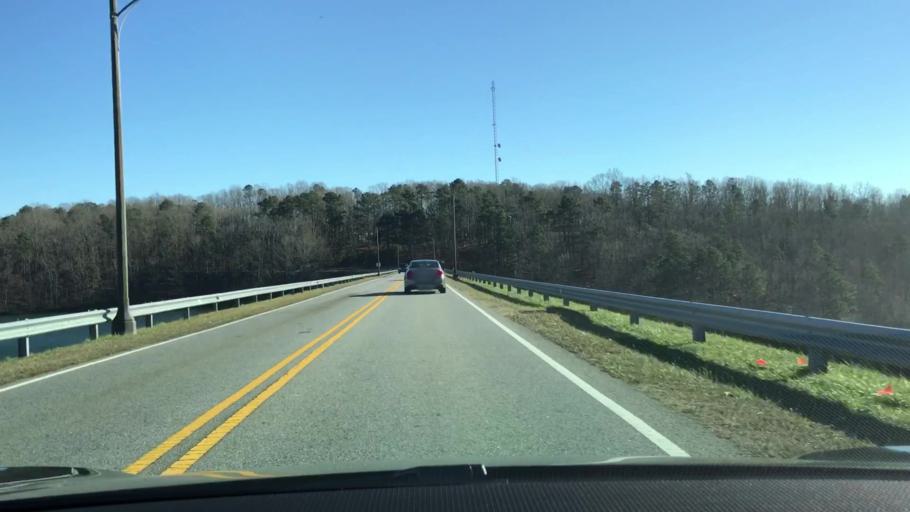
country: US
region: Georgia
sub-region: Gwinnett County
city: Sugar Hill
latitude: 34.1606
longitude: -84.0741
